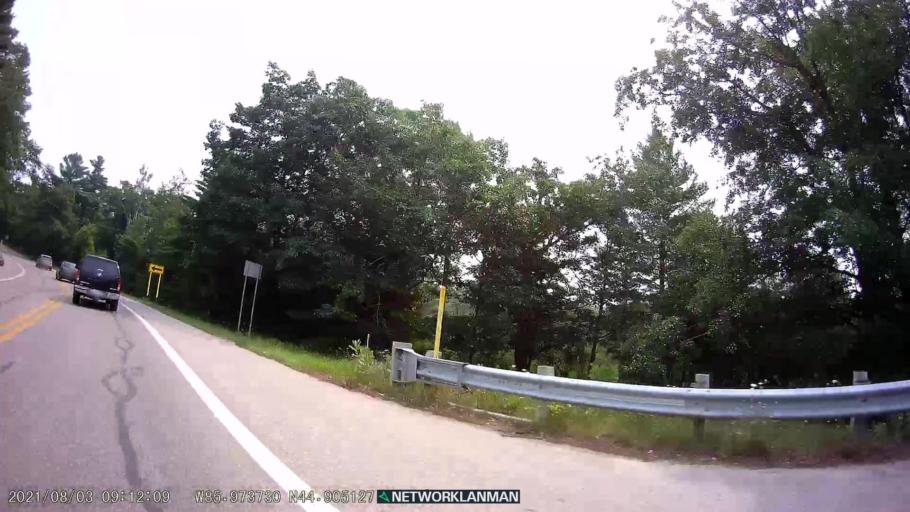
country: US
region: Michigan
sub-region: Leelanau County
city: Leland
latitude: 44.9052
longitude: -85.9736
